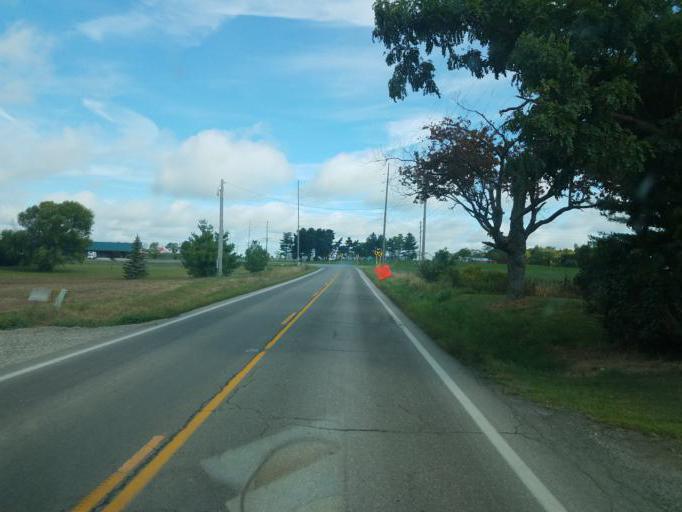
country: US
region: Ohio
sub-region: Wayne County
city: West Salem
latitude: 40.9905
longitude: -82.1100
